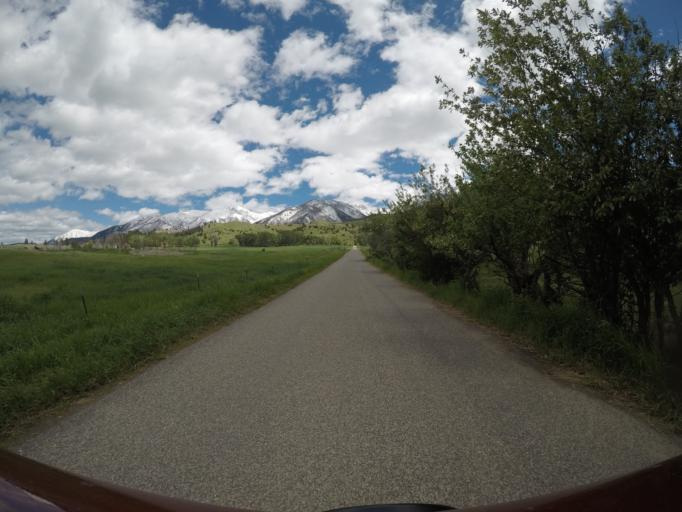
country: US
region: Montana
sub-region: Park County
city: Livingston
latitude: 45.4967
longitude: -110.5669
